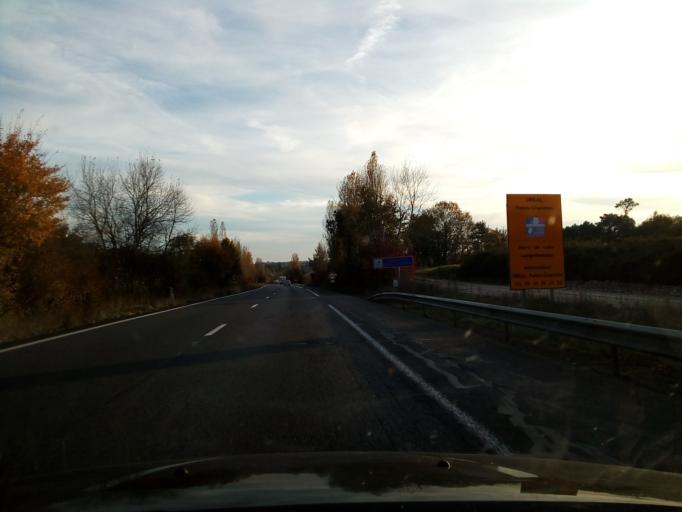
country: FR
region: Poitou-Charentes
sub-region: Departement de la Charente-Maritime
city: Chevanceaux
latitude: 45.3222
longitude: -0.2290
